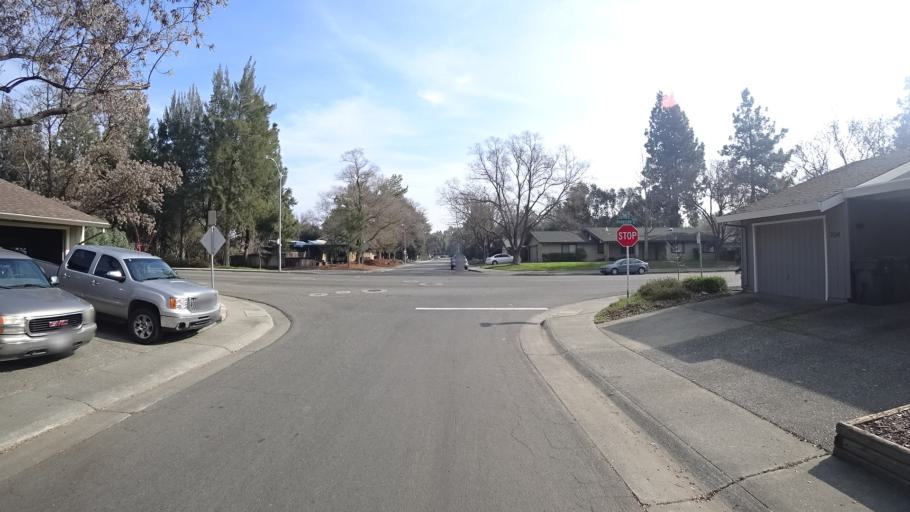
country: US
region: California
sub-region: Yolo County
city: Davis
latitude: 38.5639
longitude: -121.7587
